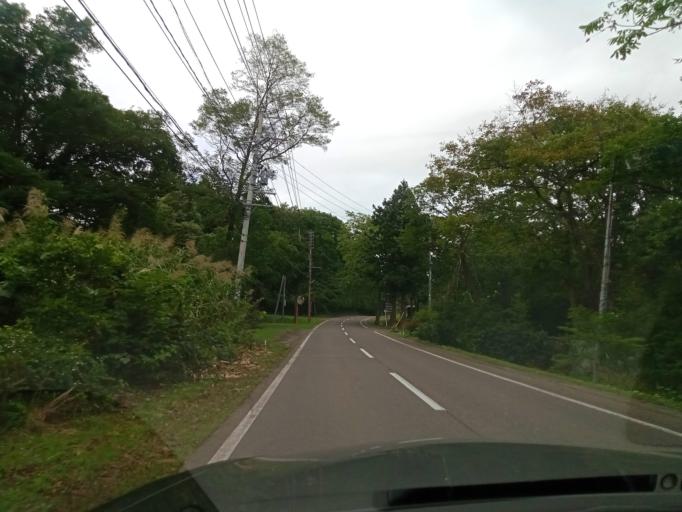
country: JP
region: Niigata
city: Arai
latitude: 36.8812
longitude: 138.1812
